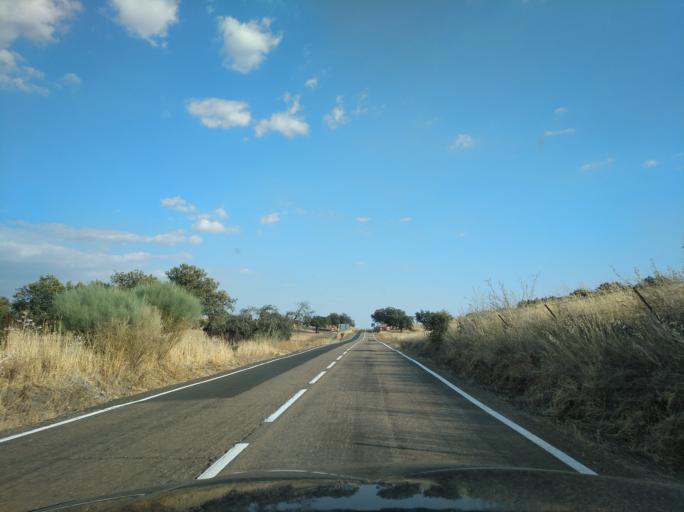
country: PT
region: Portalegre
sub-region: Campo Maior
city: Campo Maior
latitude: 39.1187
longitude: -7.0564
